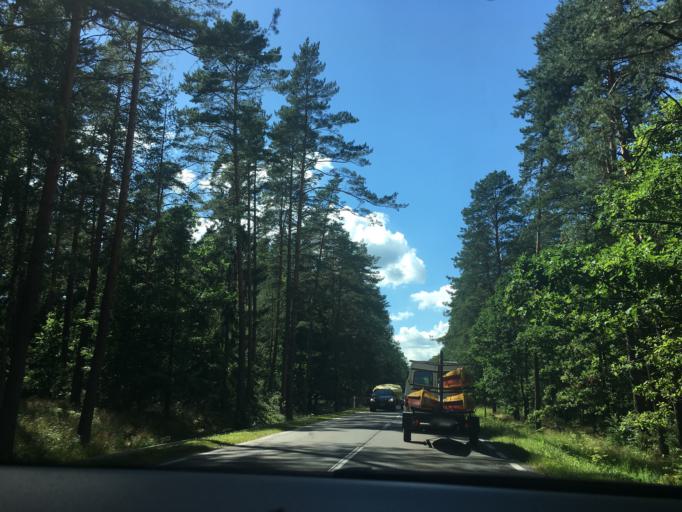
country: PL
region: Podlasie
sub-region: Powiat augustowski
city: Augustow
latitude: 53.8471
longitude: 23.0358
